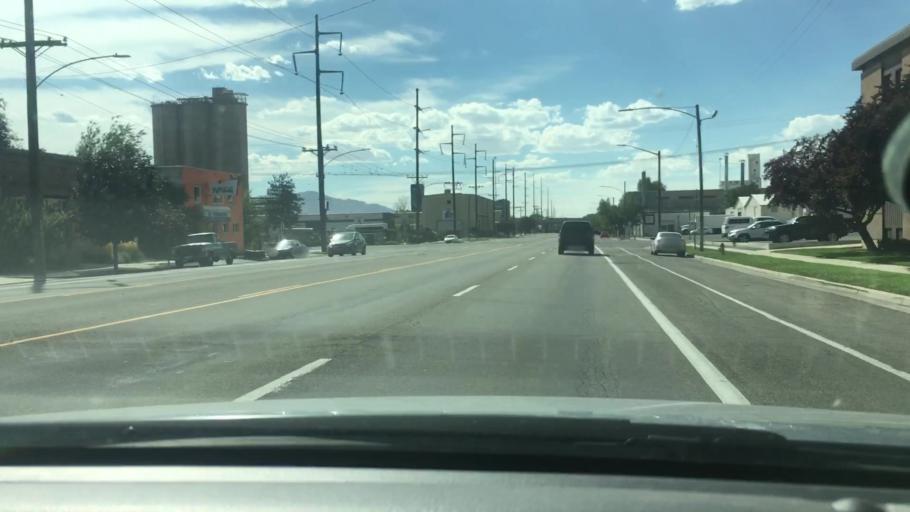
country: US
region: Utah
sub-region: Salt Lake County
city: Salt Lake City
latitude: 40.7520
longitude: -111.9042
